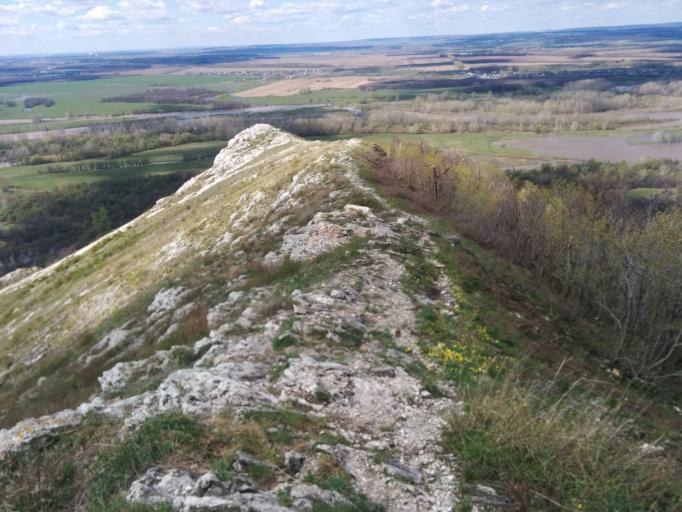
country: RU
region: Bashkortostan
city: Sterlitamak
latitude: 53.7418
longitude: 56.0965
